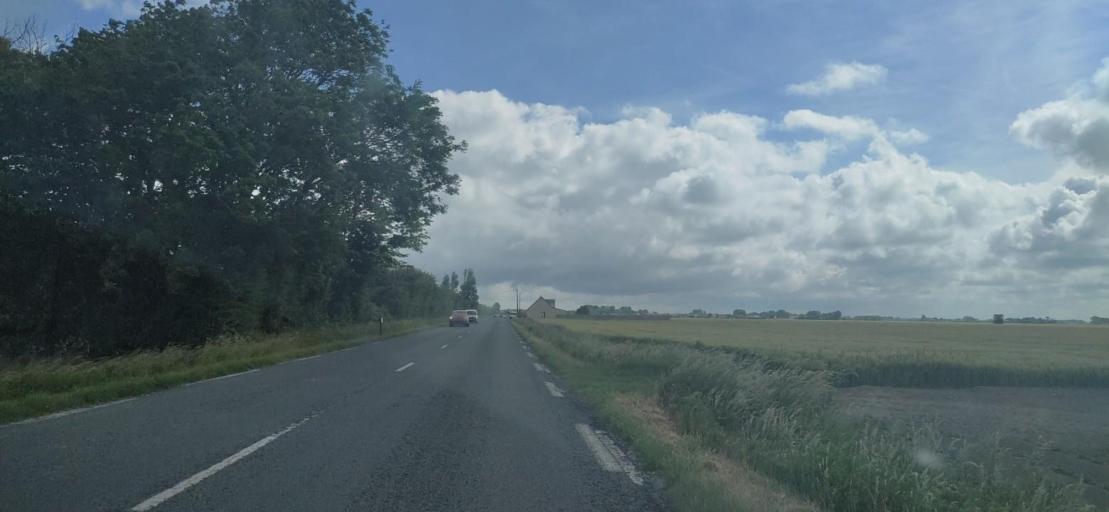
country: FR
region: Nord-Pas-de-Calais
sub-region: Departement du Pas-de-Calais
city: Oye-Plage
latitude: 50.9680
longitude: 2.0156
